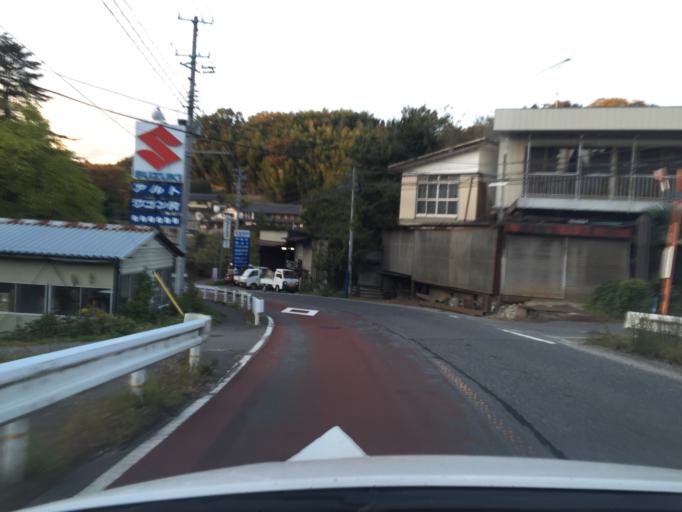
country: JP
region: Fukushima
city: Koriyama
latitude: 37.3681
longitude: 140.4474
